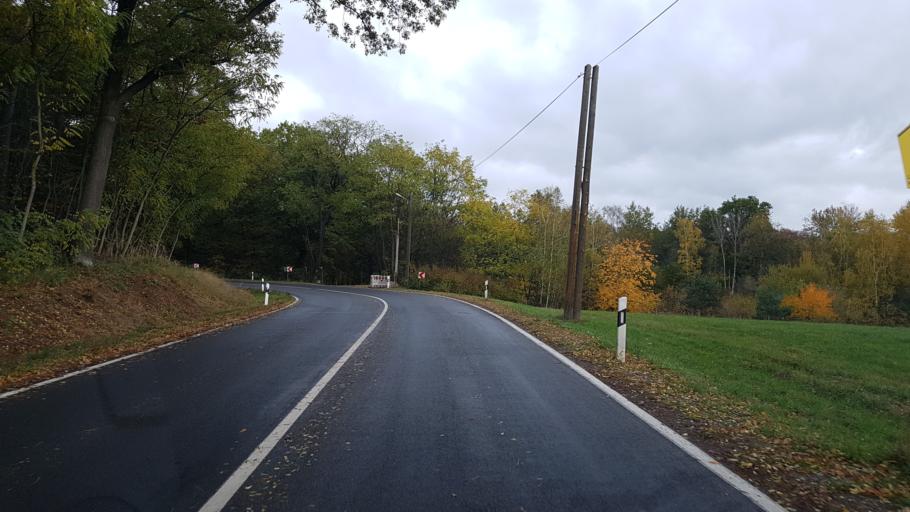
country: DE
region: Saxony
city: Dahlen
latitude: 51.4026
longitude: 12.9825
